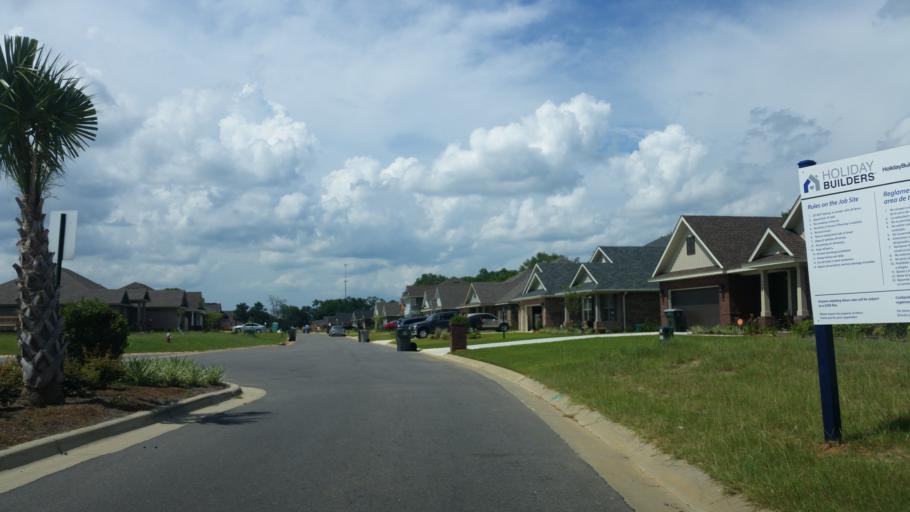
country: US
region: Florida
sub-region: Escambia County
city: Cantonment
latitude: 30.5506
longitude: -87.3703
